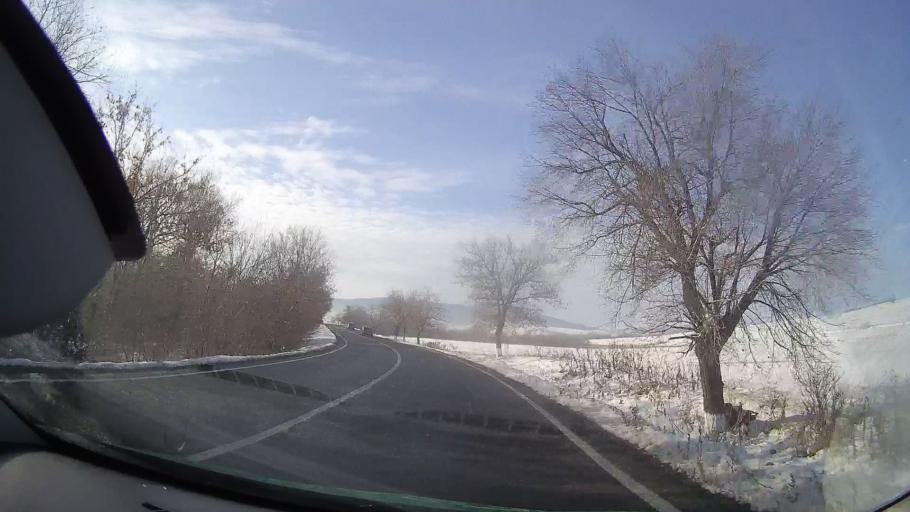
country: RO
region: Neamt
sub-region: Comuna Negresti
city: Negresti
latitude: 46.9982
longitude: 26.3809
